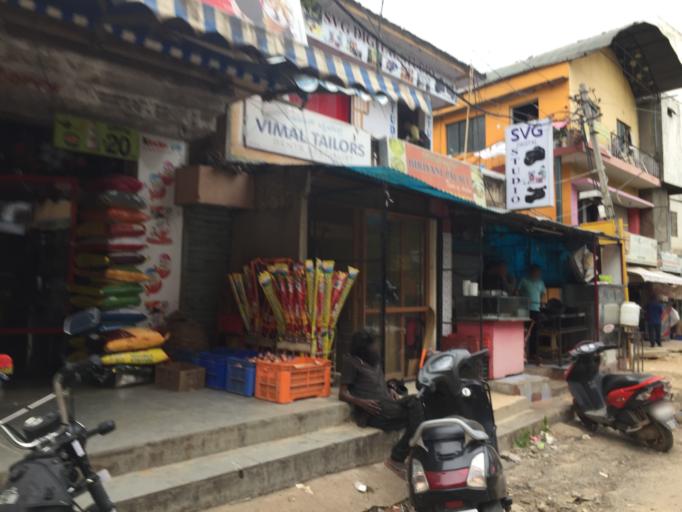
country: IN
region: Karnataka
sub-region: Bangalore Urban
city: Bangalore
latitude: 12.9649
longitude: 77.6574
